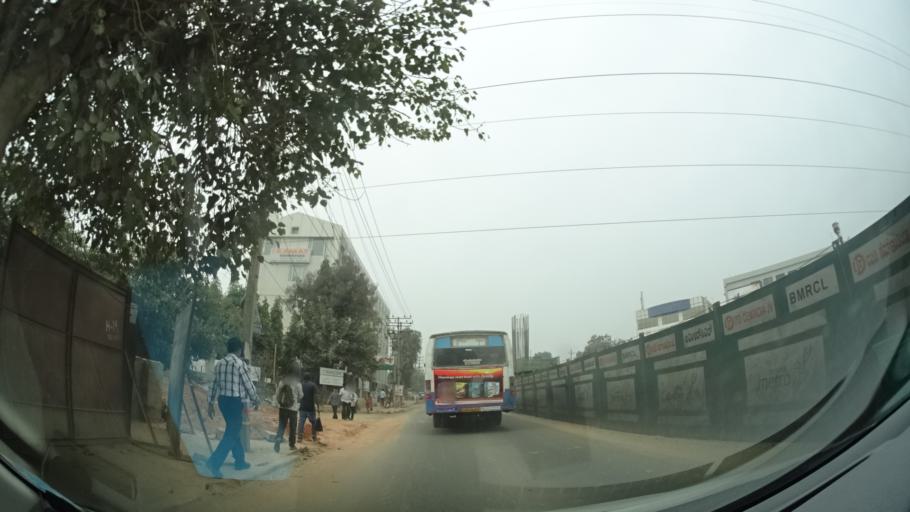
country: IN
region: Karnataka
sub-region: Bangalore Rural
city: Hoskote
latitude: 12.9901
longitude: 77.7135
